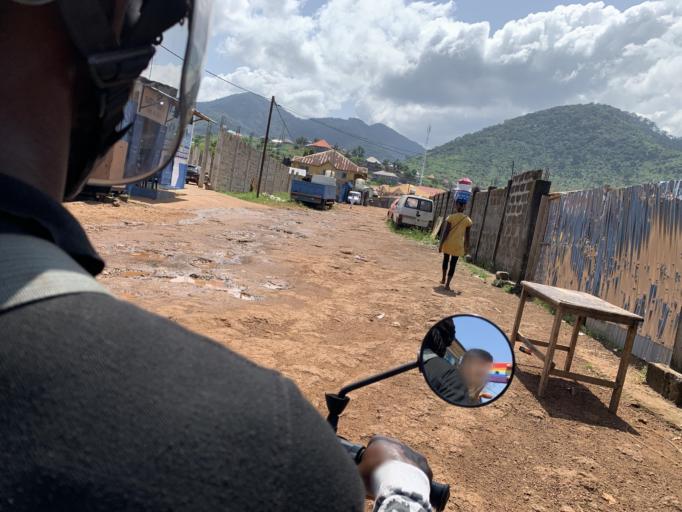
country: SL
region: Western Area
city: Hastings
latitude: 8.3749
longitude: -13.1327
